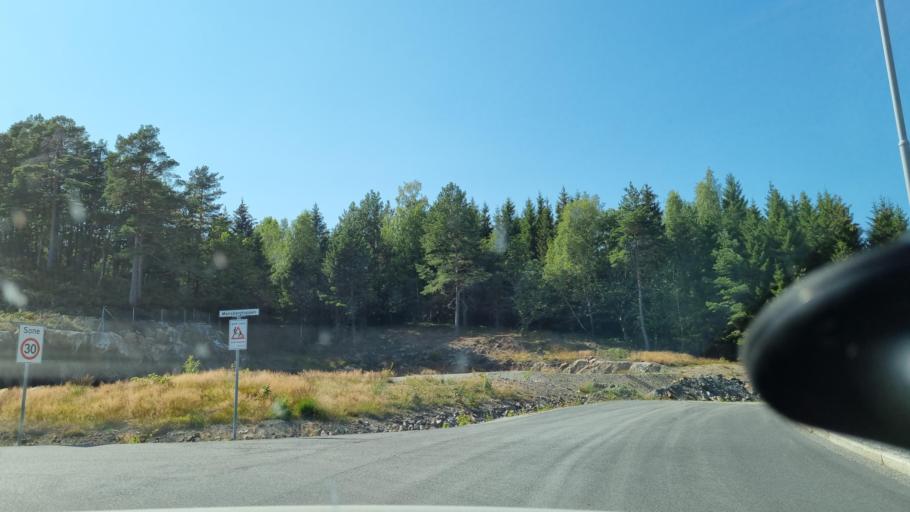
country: NO
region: Aust-Agder
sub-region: Arendal
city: Arendal
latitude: 58.4606
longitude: 8.8146
